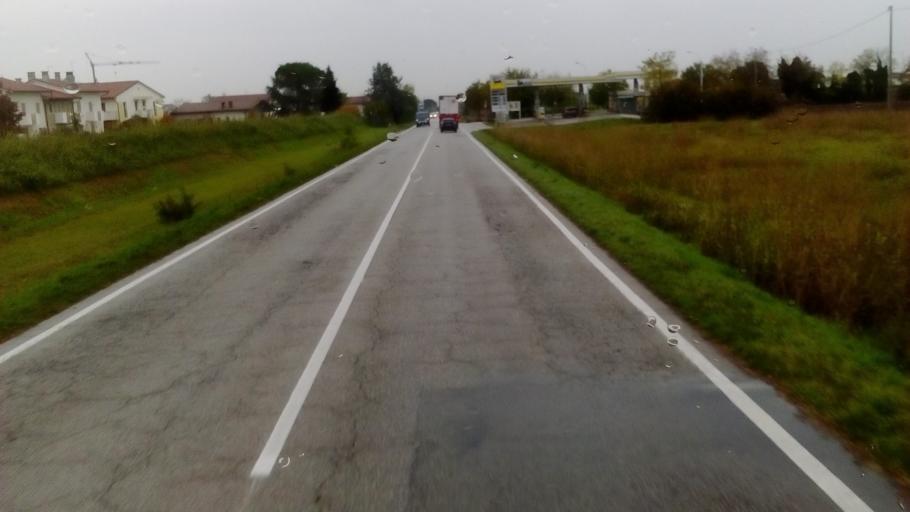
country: IT
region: Veneto
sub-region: Provincia di Vicenza
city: Breganze
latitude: 45.6857
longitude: 11.5649
